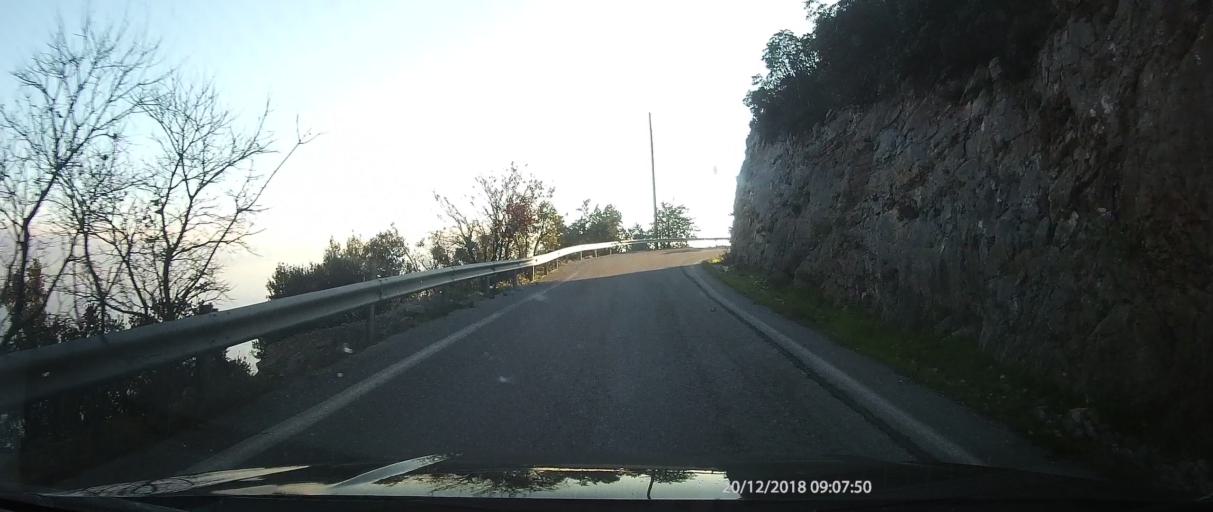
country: GR
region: Peloponnese
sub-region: Nomos Lakonias
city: Sykea
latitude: 36.9249
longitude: 23.0079
